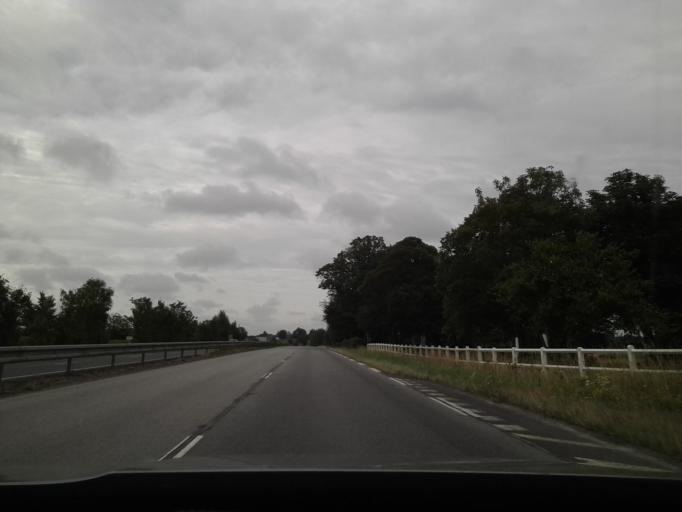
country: FR
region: Lower Normandy
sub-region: Departement de la Manche
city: Carentan
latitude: 49.3532
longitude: -1.2774
